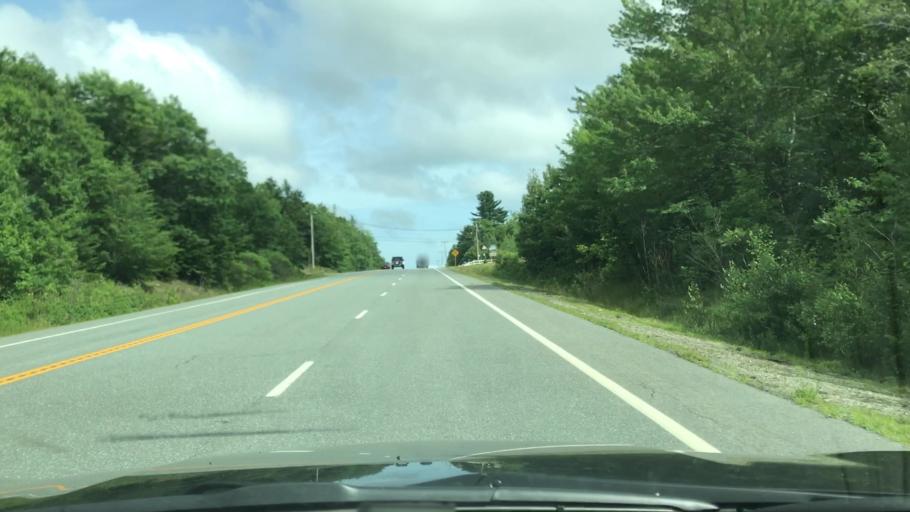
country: US
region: Maine
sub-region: Hancock County
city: Surry
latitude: 44.5548
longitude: -68.5397
